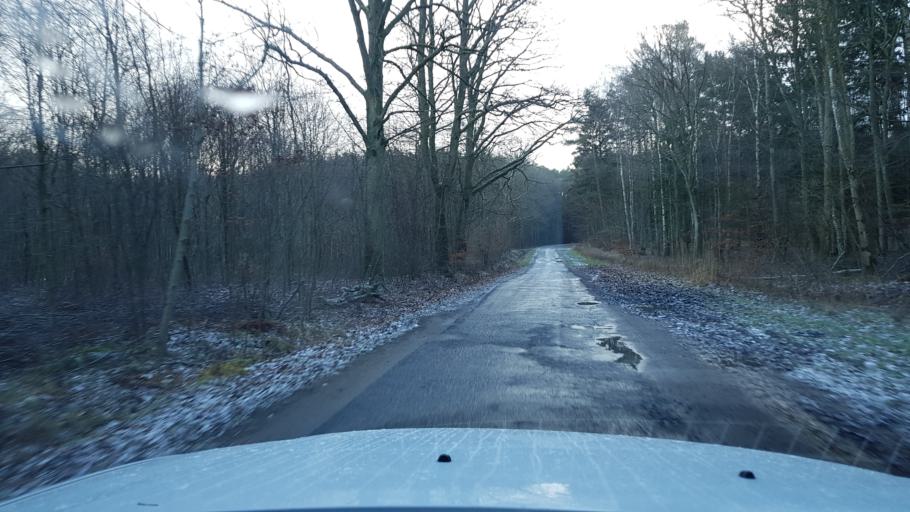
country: PL
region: West Pomeranian Voivodeship
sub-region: Powiat gryficki
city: Trzebiatow
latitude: 54.0465
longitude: 15.3254
